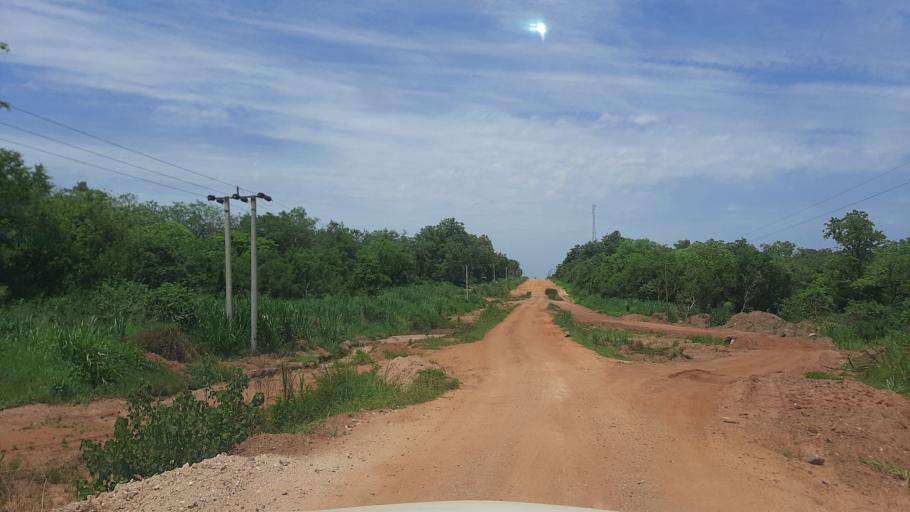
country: ET
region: Gambela
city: Gambela
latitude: 8.0673
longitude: 34.5872
